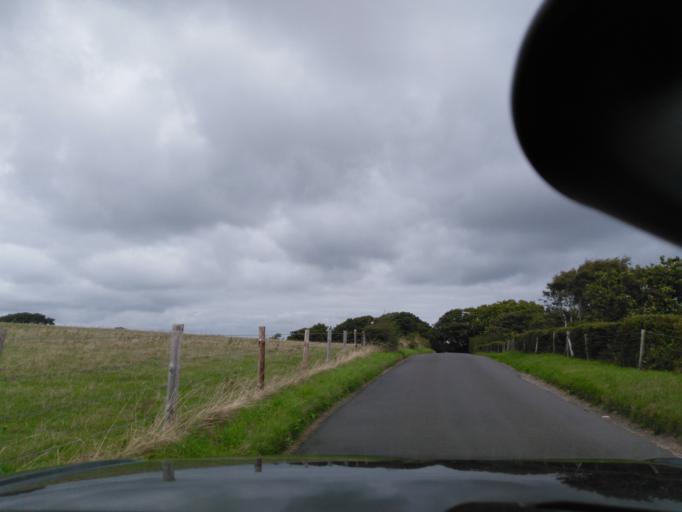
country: GB
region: England
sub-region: Dorset
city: Swanage
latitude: 50.6349
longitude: -1.9833
